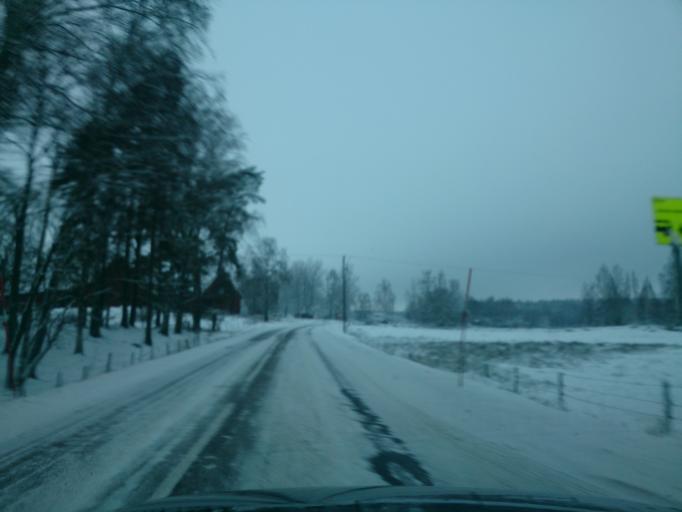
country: SE
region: OEstergoetland
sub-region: Norrkopings Kommun
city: Kimstad
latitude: 58.4257
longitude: 15.9081
